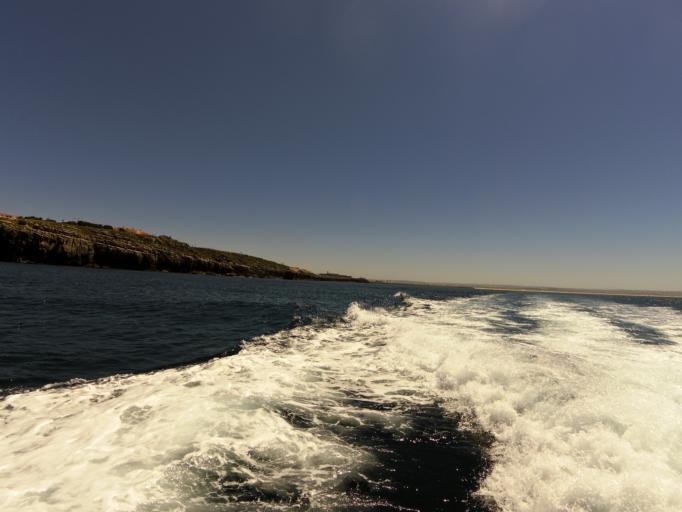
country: PT
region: Leiria
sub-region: Peniche
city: Peniche
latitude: 39.3520
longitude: -9.3951
